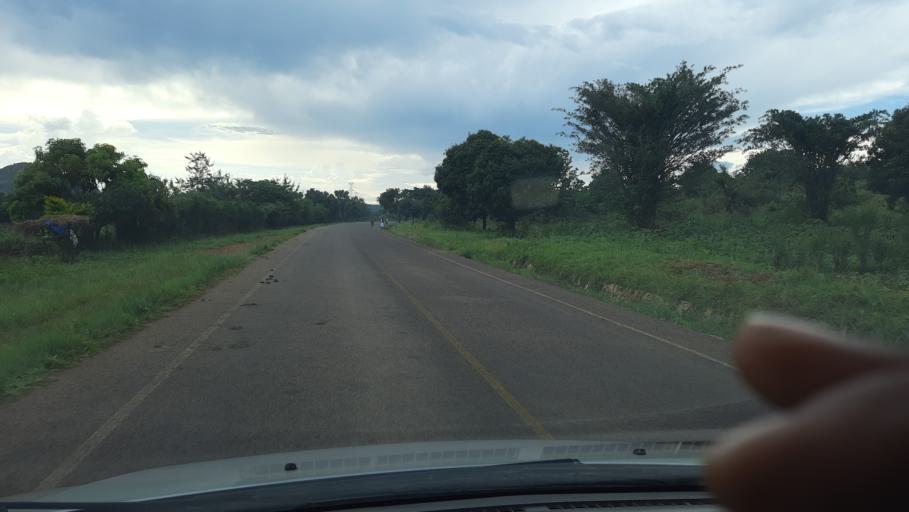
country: UG
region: Central Region
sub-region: Nakasongola District
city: Nakasongola
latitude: 1.3147
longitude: 32.4423
